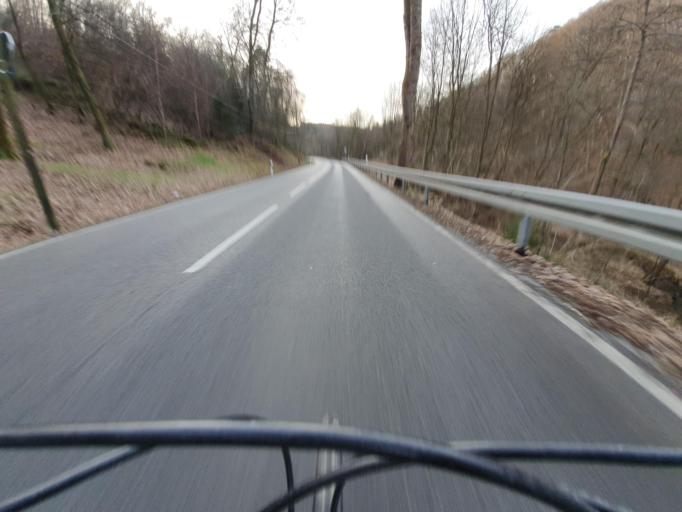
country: DE
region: North Rhine-Westphalia
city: Burscheid
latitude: 51.0891
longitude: 7.1727
